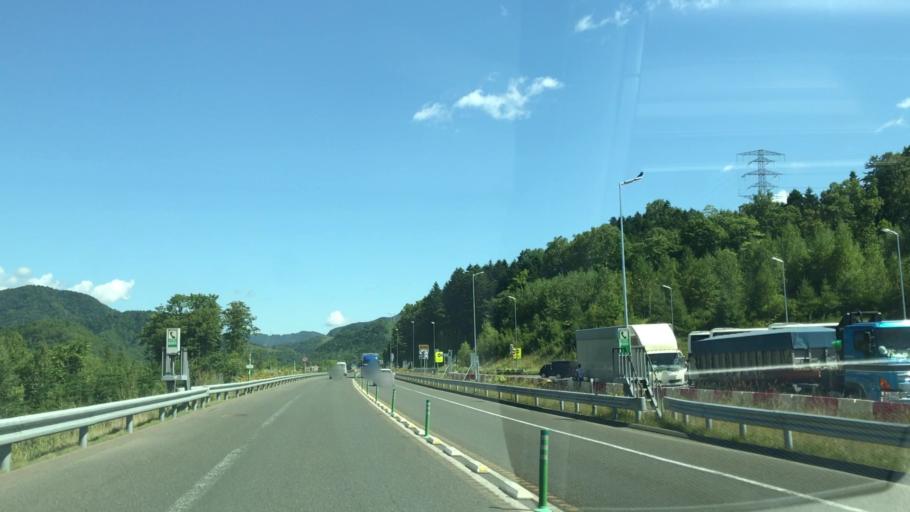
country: JP
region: Hokkaido
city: Shimo-furano
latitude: 43.0054
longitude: 142.4155
